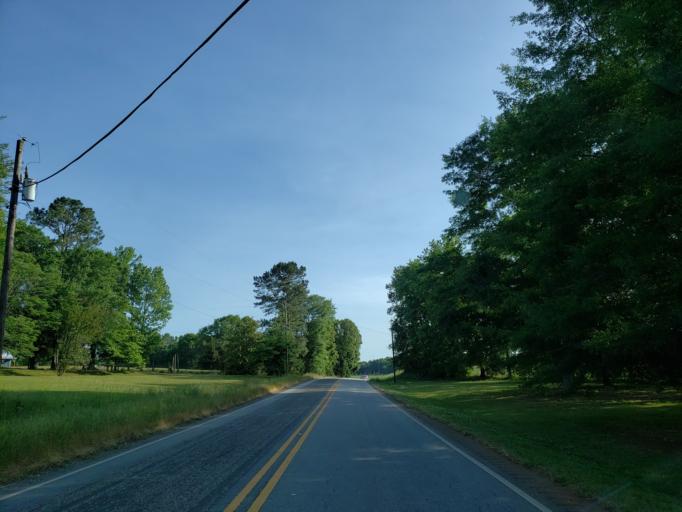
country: US
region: Georgia
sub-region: Carroll County
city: Bowdon
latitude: 33.4611
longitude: -85.3125
